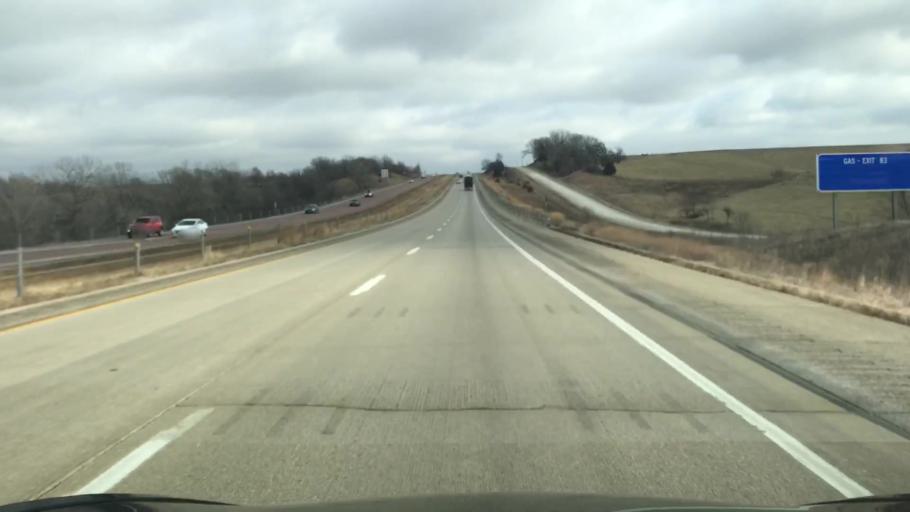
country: US
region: Iowa
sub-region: Guthrie County
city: Guthrie Center
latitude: 41.4962
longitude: -94.5362
